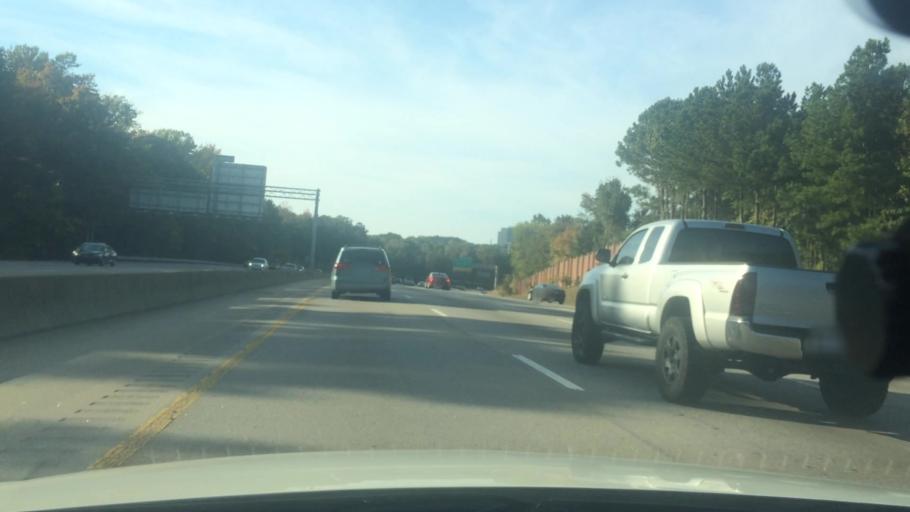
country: US
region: North Carolina
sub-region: Wake County
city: Raleigh
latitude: 35.8264
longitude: -78.6237
